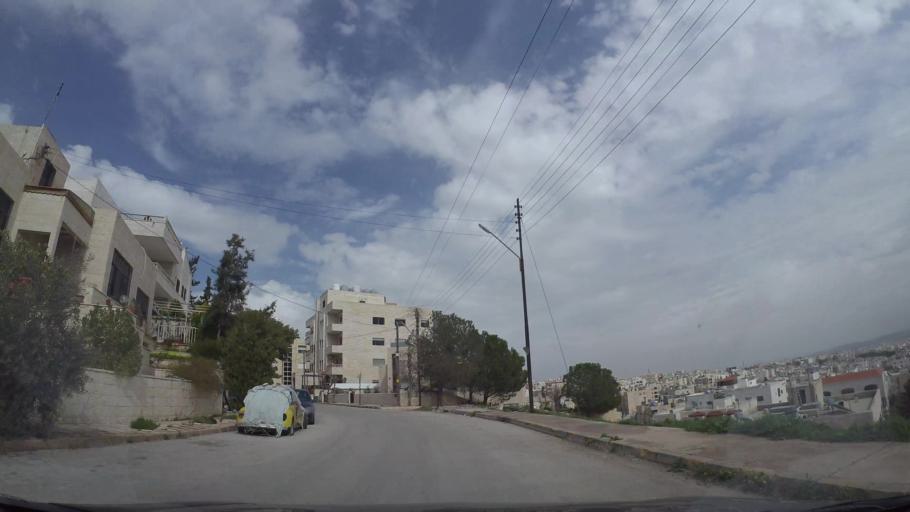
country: JO
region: Amman
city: Amman
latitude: 31.9984
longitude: 35.9358
